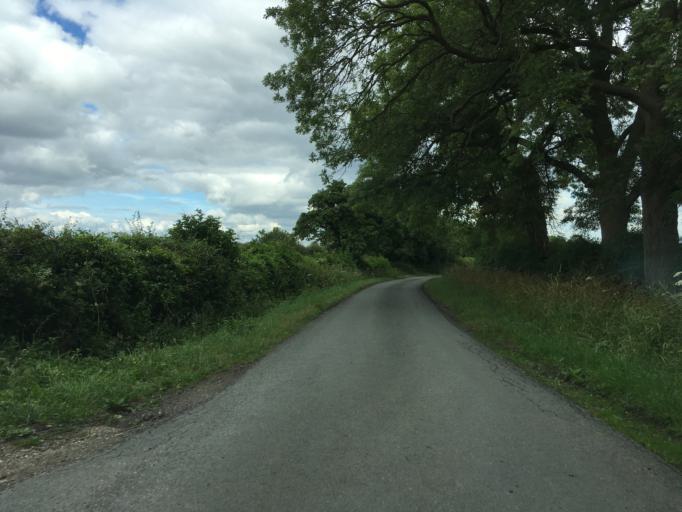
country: GB
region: England
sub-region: Gloucestershire
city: Stonehouse
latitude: 51.7947
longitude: -2.3866
